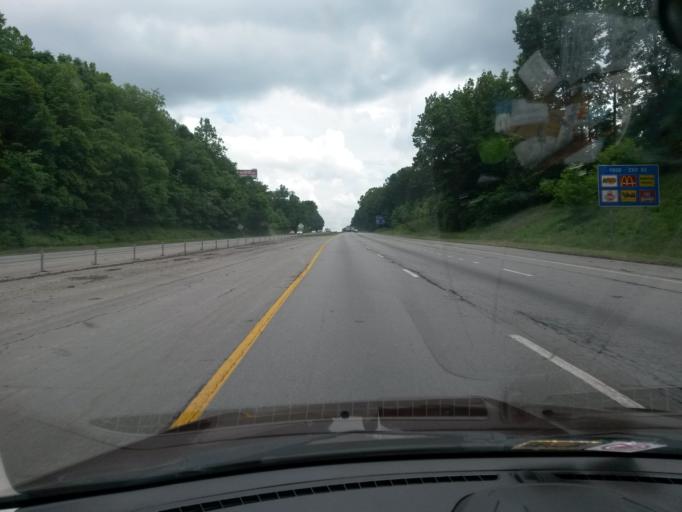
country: US
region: North Carolina
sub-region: Yadkin County
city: Jonesville
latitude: 36.2482
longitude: -80.8205
